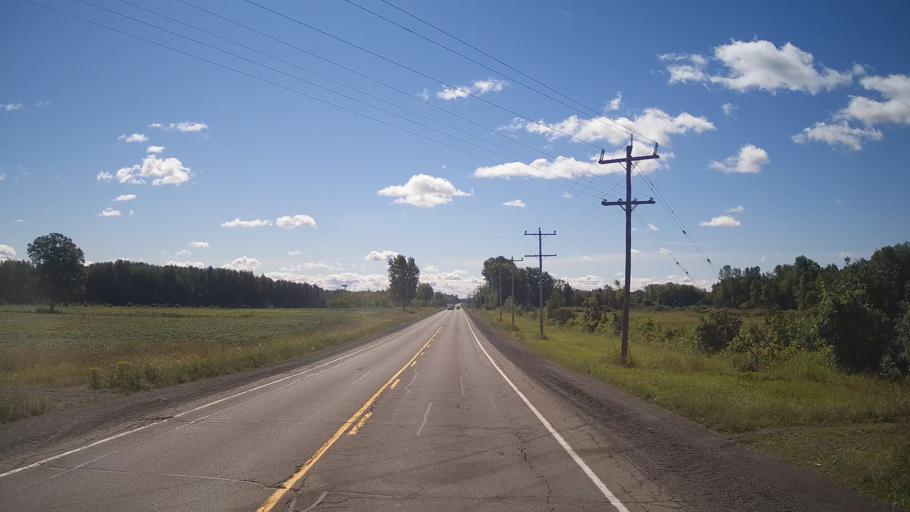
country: US
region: New York
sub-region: St. Lawrence County
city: Norfolk
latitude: 44.9566
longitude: -75.2289
